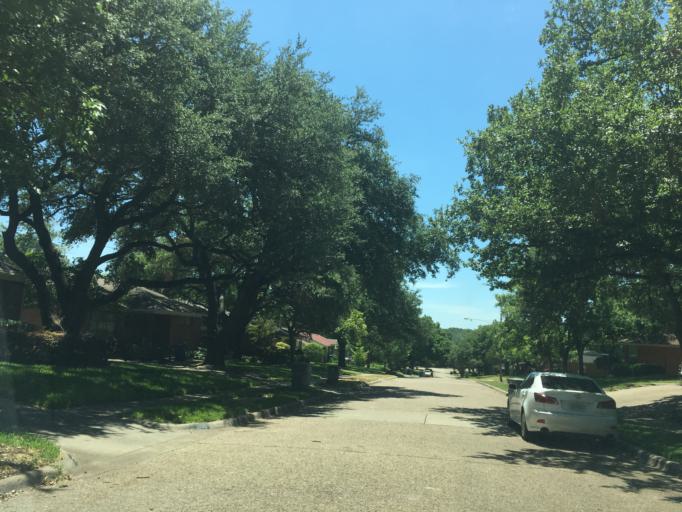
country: US
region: Texas
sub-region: Dallas County
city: Highland Park
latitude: 32.8502
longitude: -96.7053
